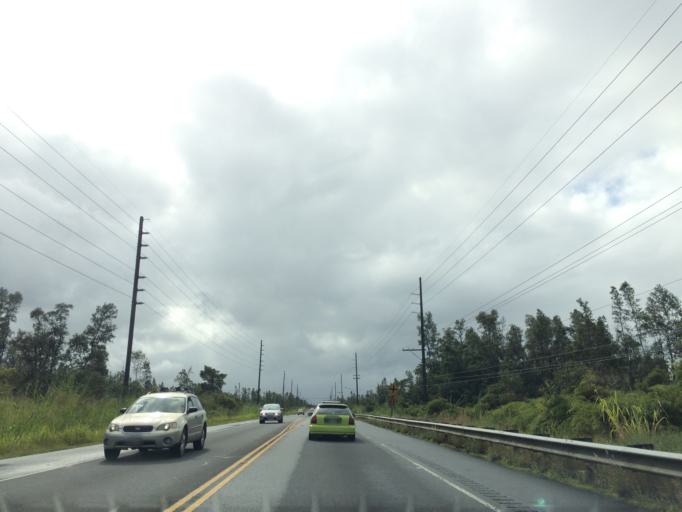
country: US
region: Hawaii
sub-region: Hawaii County
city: Hawaiian Paradise Park
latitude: 19.5223
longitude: -154.9684
